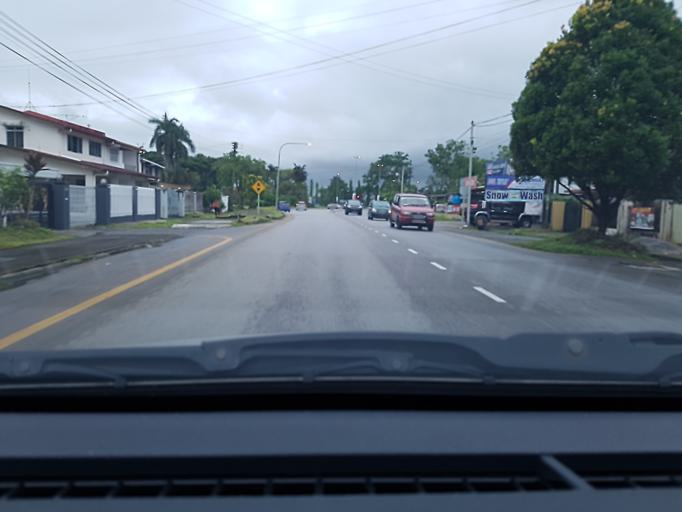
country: MY
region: Sarawak
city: Kuching
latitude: 1.5251
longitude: 110.3724
